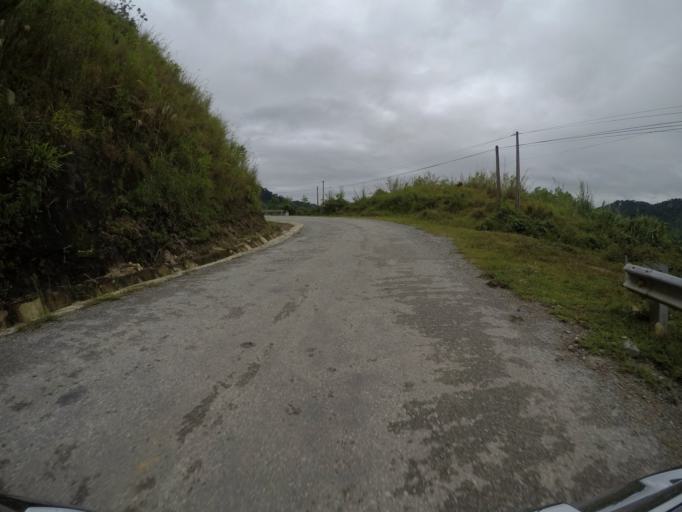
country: VN
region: Quang Nam
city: Thanh My
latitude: 15.6751
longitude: 107.6516
